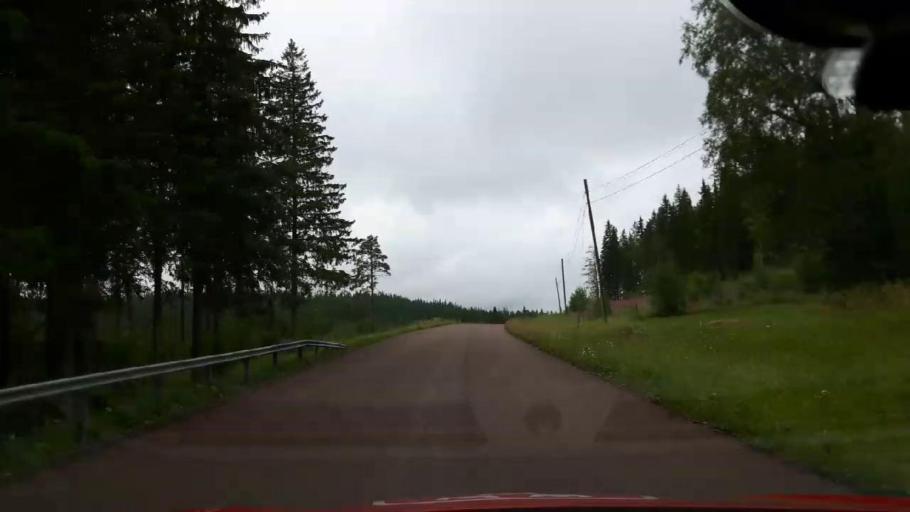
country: SE
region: Jaemtland
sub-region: Krokoms Kommun
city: Valla
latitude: 63.3896
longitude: 13.8547
